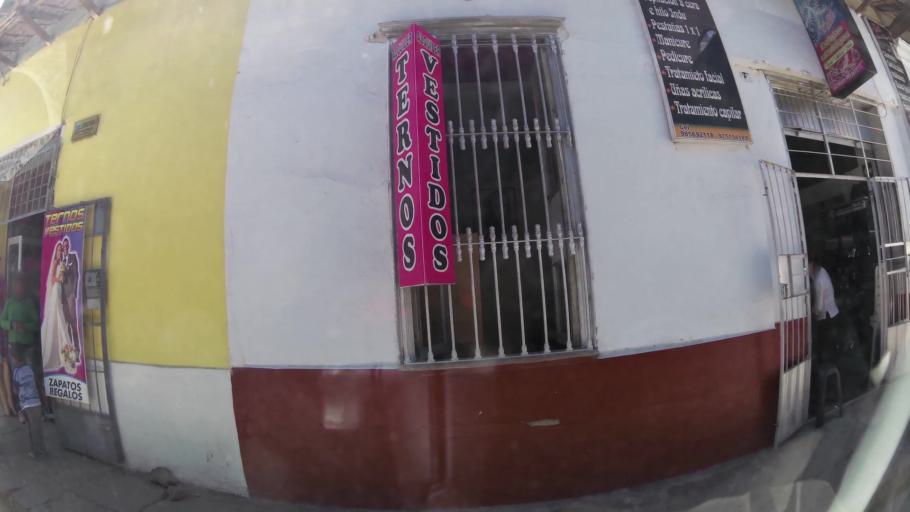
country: PE
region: Junin
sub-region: Provincia de Jauja
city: Jauja
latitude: -11.7742
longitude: -75.4991
